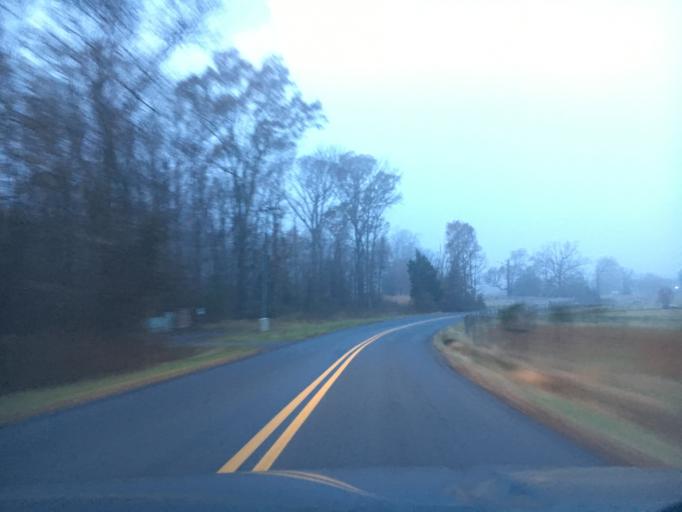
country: US
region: Virginia
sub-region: Halifax County
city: Mountain Road
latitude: 36.6795
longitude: -79.0257
